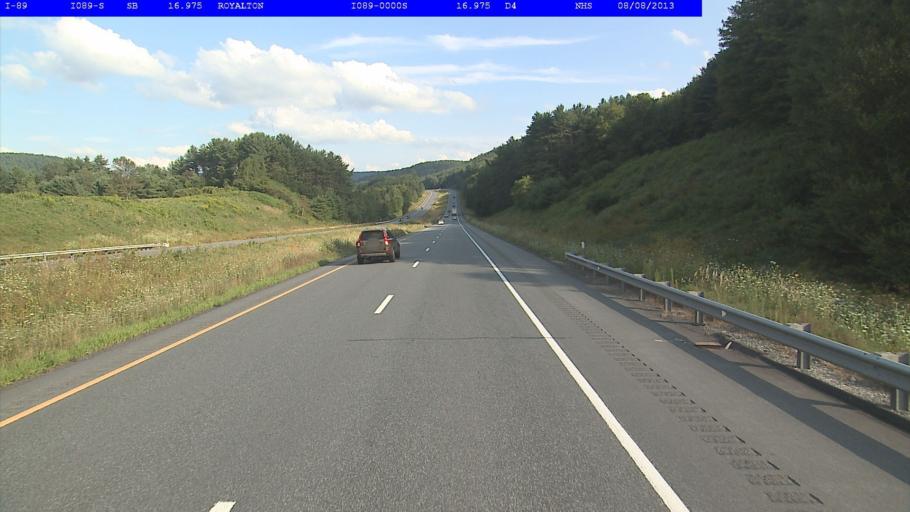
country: US
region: Vermont
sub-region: Windsor County
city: Woodstock
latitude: 43.8012
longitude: -72.5120
